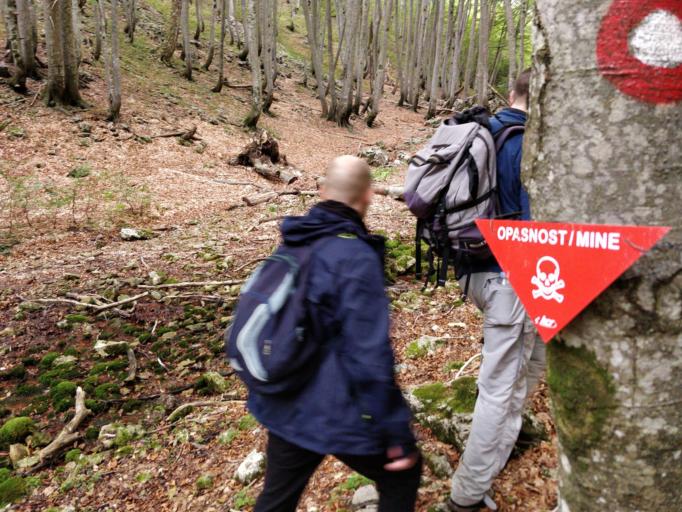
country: HR
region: Zadarska
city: Starigrad
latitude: 44.3745
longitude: 15.5050
